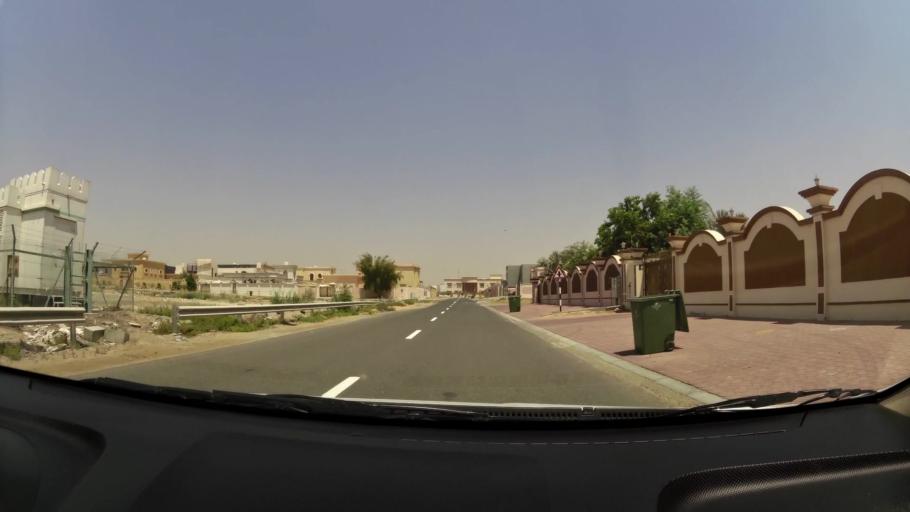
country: AE
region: Ajman
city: Ajman
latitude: 25.4219
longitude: 55.5126
